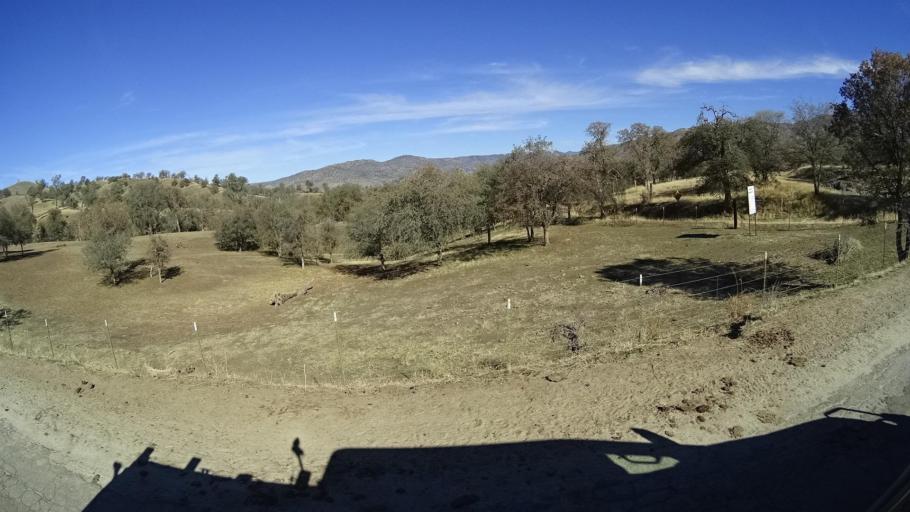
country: US
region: California
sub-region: Kern County
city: Arvin
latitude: 35.4419
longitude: -118.7154
